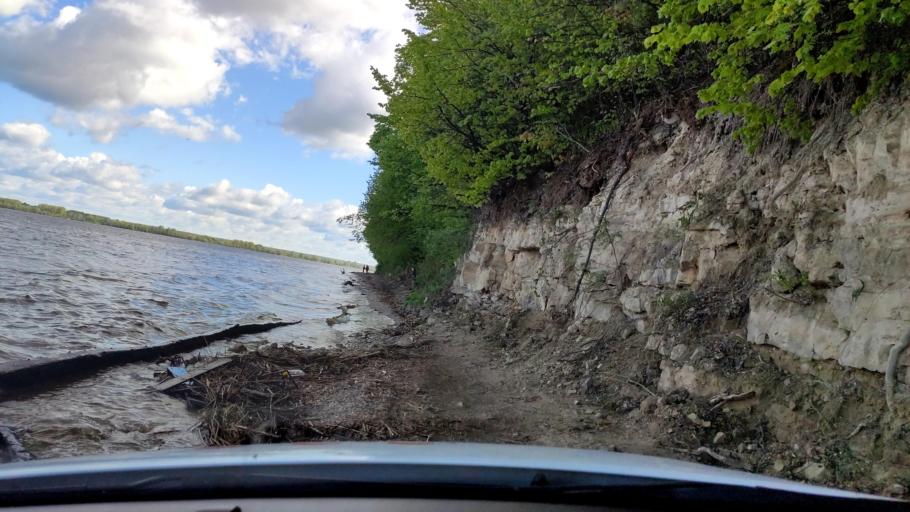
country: RU
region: Tatarstan
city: Sviyazhsk
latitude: 55.7796
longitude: 48.6953
